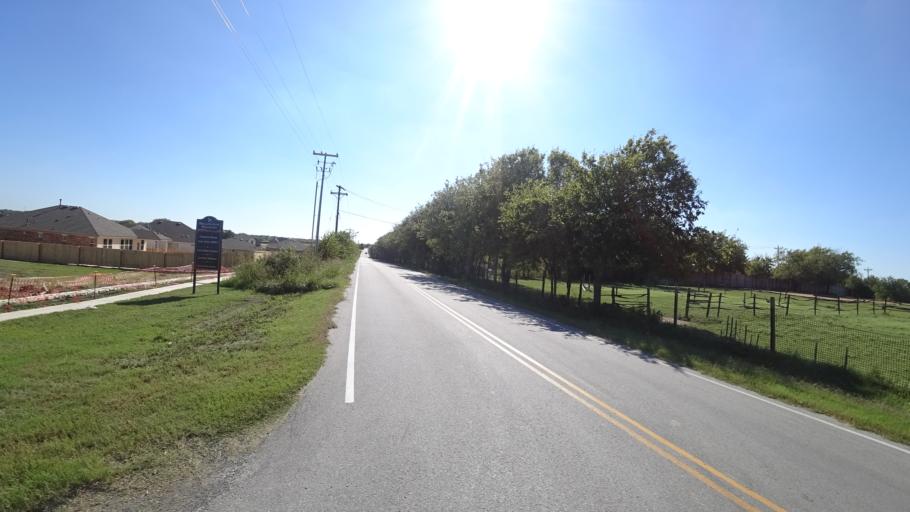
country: US
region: Texas
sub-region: Travis County
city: Manor
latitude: 30.3574
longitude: -97.6070
